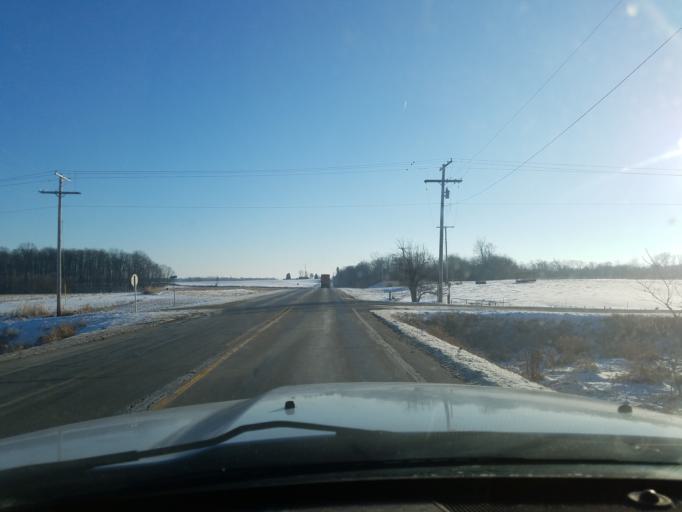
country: US
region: Indiana
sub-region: Noble County
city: Albion
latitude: 41.4531
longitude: -85.4625
